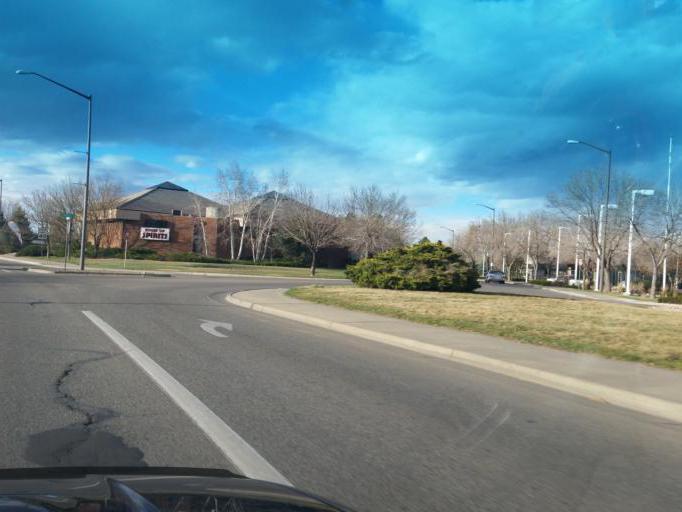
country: US
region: Colorado
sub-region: Larimer County
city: Loveland
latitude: 40.4187
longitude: -105.0733
